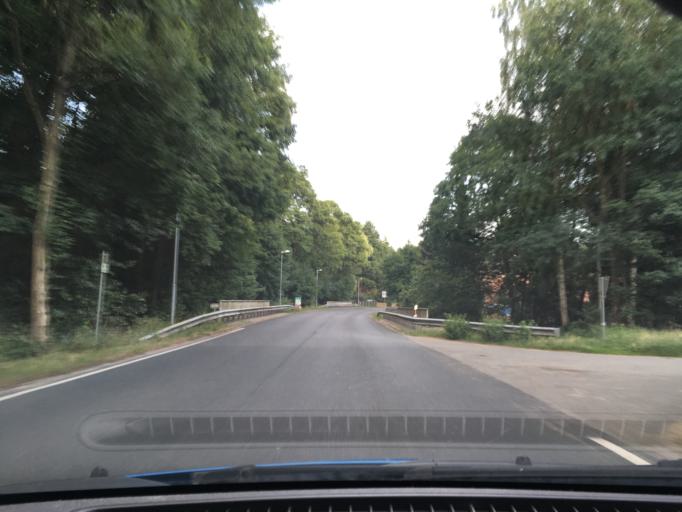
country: DE
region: Lower Saxony
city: Eldingen
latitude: 52.6906
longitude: 10.3340
